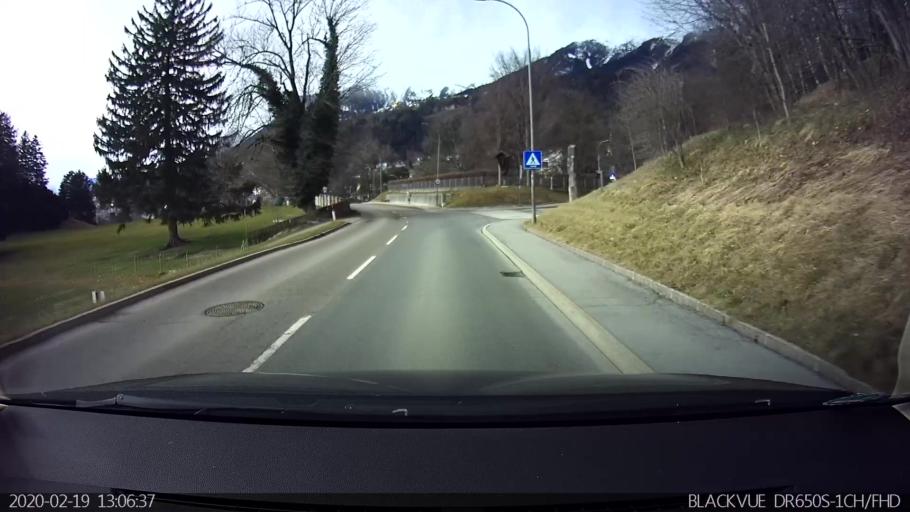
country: AT
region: Tyrol
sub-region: Innsbruck Stadt
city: Innsbruck
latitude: 47.2821
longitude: 11.4167
